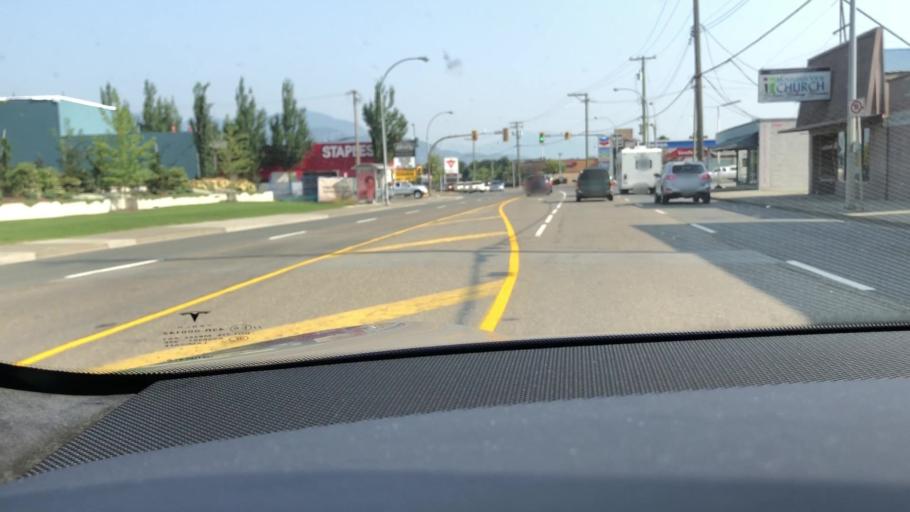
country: CA
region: British Columbia
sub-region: Fraser Valley Regional District
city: Chilliwack
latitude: 49.1372
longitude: -121.9589
